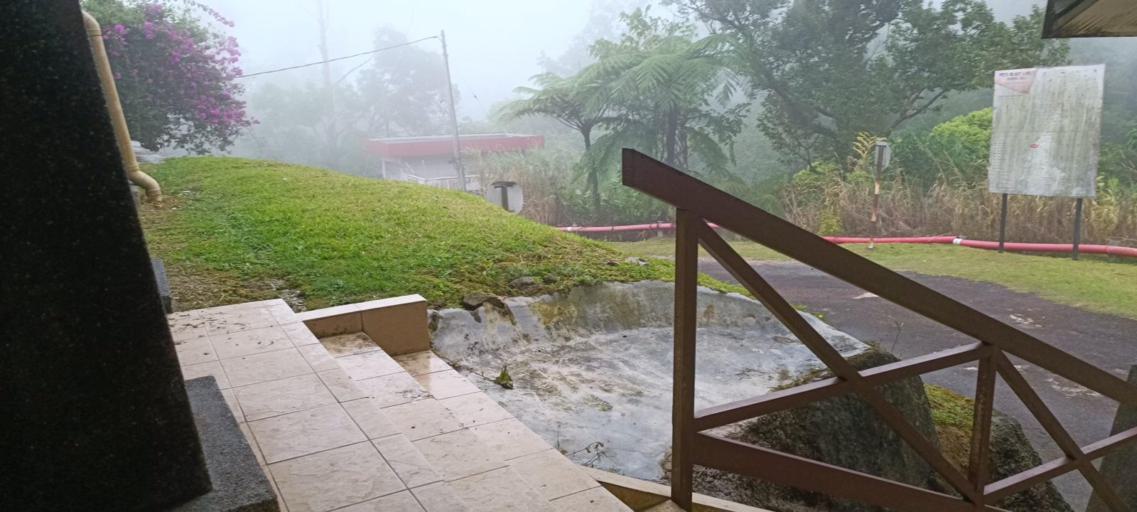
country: MY
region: Perak
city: Taiping
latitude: 4.8670
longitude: 100.7775
